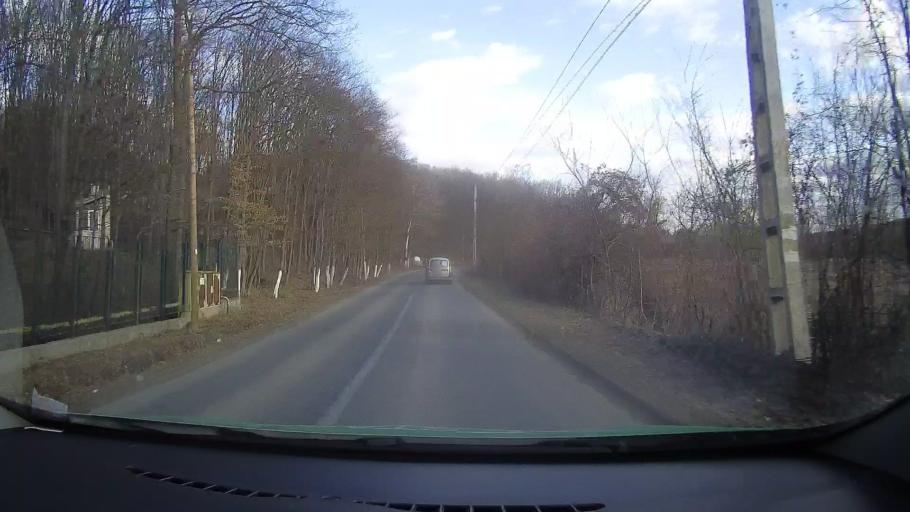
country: RO
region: Dambovita
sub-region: Comuna Gura Ocnitei
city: Gura Ocnitei
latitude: 44.9568
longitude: 25.5508
